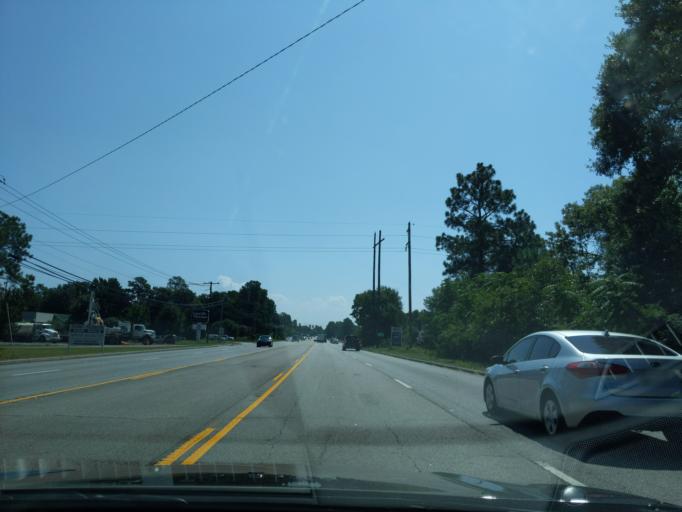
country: US
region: South Carolina
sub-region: Lexington County
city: Oak Grove
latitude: 33.9750
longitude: -81.1732
